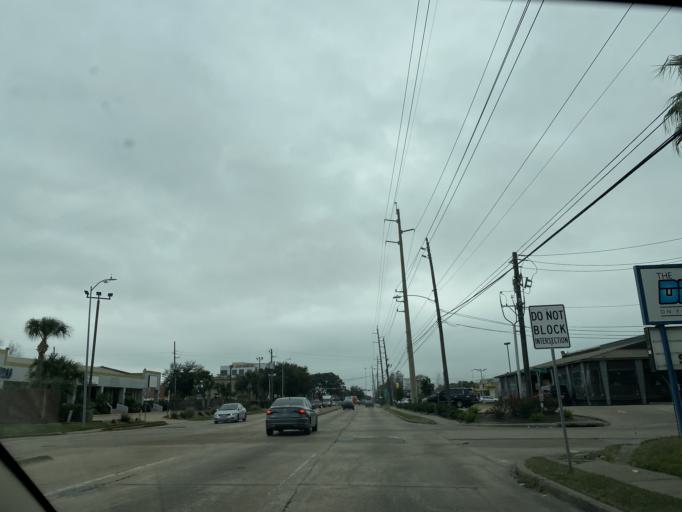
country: US
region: Texas
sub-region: Harris County
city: Bellaire
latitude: 29.7333
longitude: -95.4843
